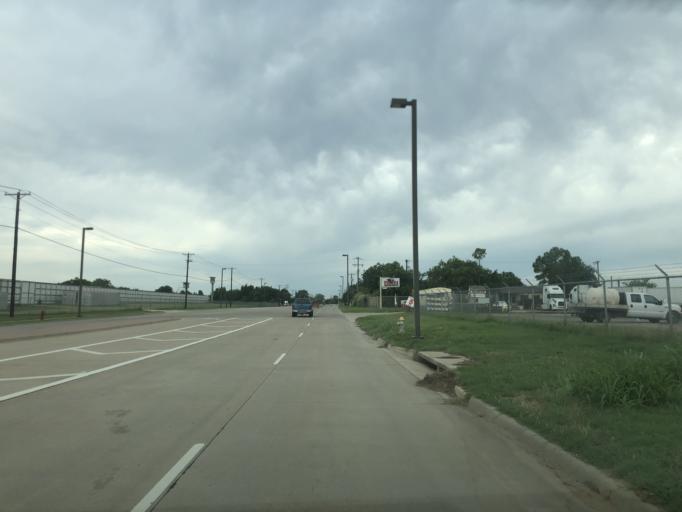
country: US
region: Texas
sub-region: Dallas County
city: Grand Prairie
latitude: 32.7779
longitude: -96.9880
